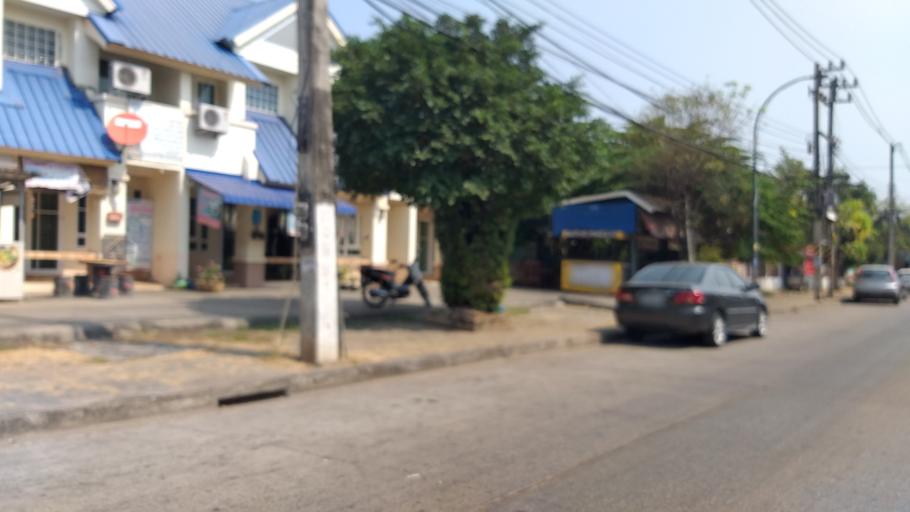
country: TH
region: Changwat Udon Thani
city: Udon Thani
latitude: 17.4040
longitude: 102.7831
